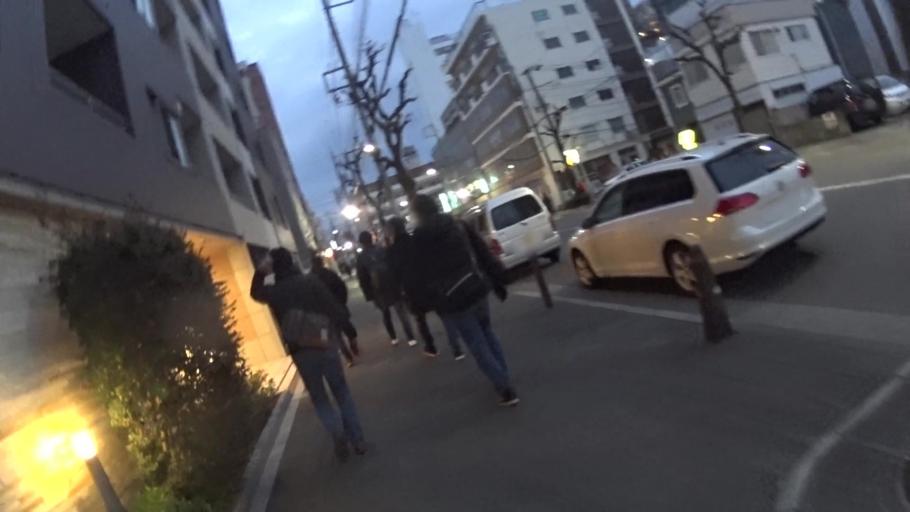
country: JP
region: Kanagawa
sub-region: Kawasaki-shi
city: Kawasaki
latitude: 35.5741
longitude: 139.7049
